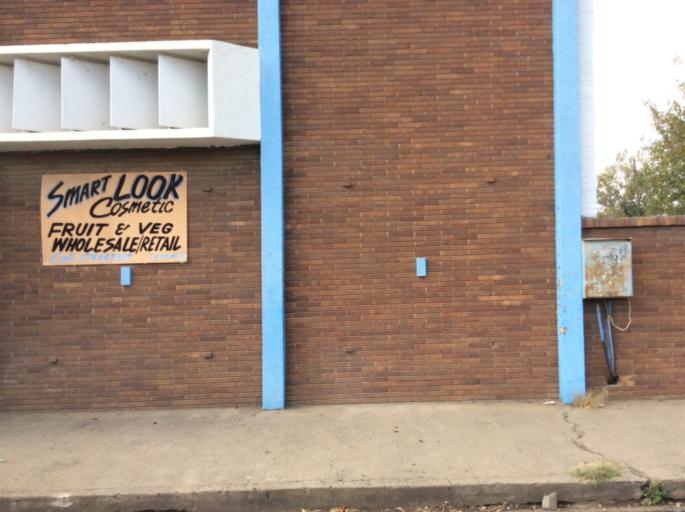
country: LS
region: Mafeteng
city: Mafeteng
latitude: -29.7280
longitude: 27.0389
